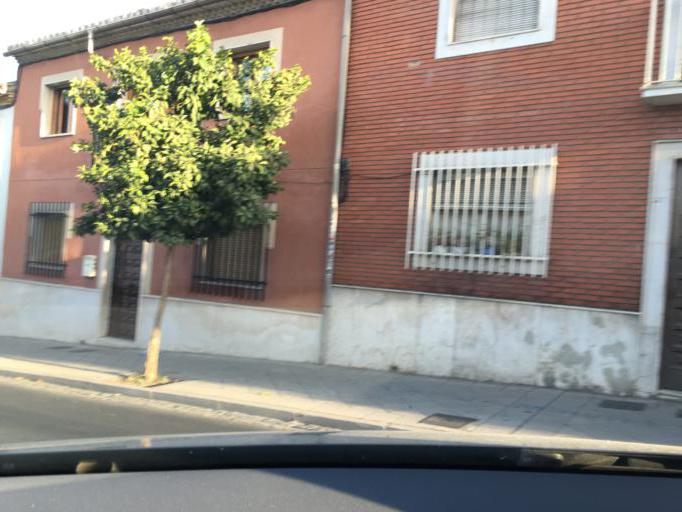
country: ES
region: Andalusia
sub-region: Provincia de Granada
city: Granada
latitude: 37.1904
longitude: -3.6013
